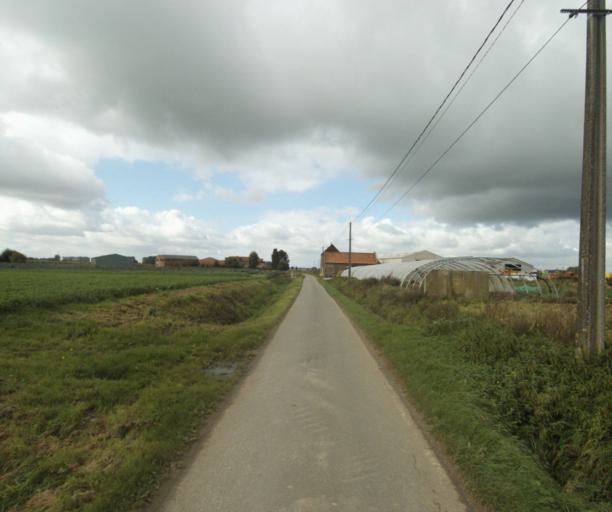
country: FR
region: Nord-Pas-de-Calais
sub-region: Departement du Nord
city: Verlinghem
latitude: 50.6941
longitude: 2.9867
